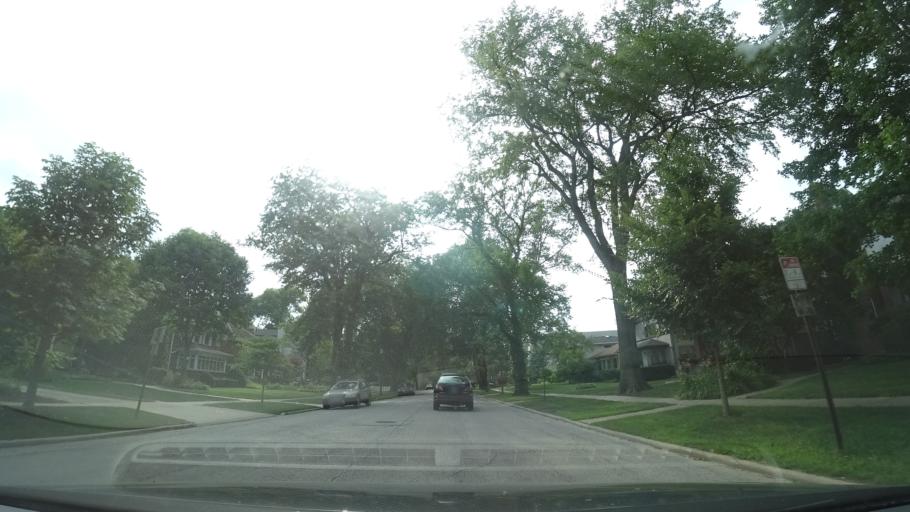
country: US
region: Illinois
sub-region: Cook County
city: Evanston
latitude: 42.0621
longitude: -87.6928
